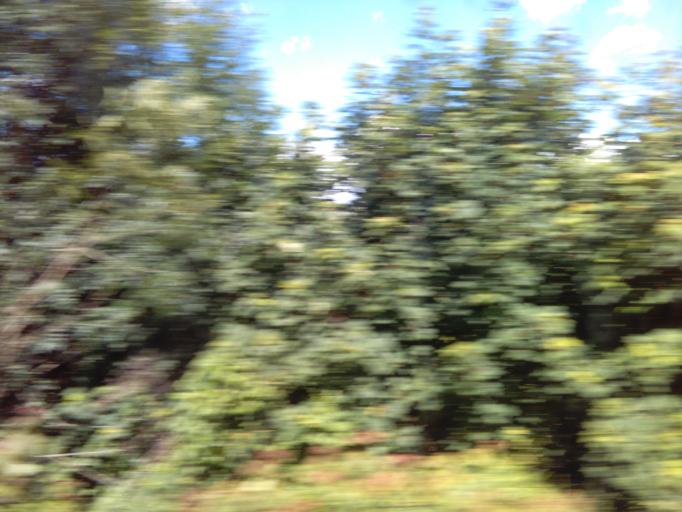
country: GB
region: England
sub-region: Luton
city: Luton
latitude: 51.8579
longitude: -0.3791
